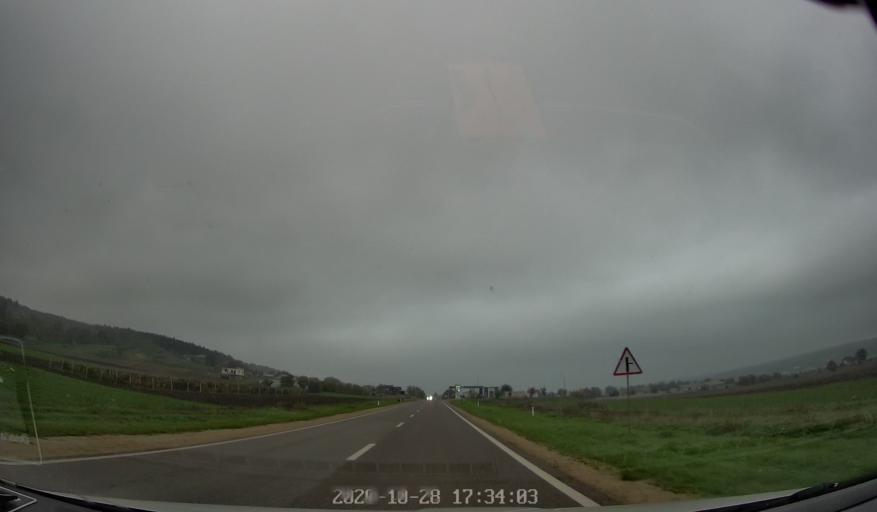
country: MD
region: Hincesti
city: Hincesti
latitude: 46.7397
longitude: 28.6523
